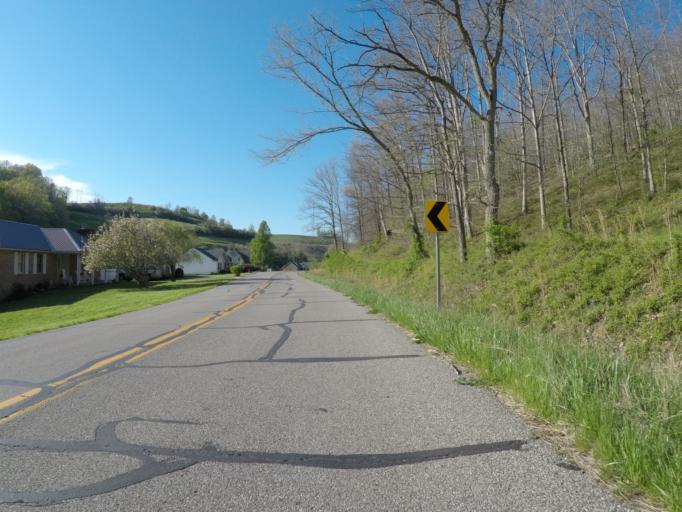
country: US
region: Kentucky
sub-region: Boyd County
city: Meads
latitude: 38.3601
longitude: -82.6882
